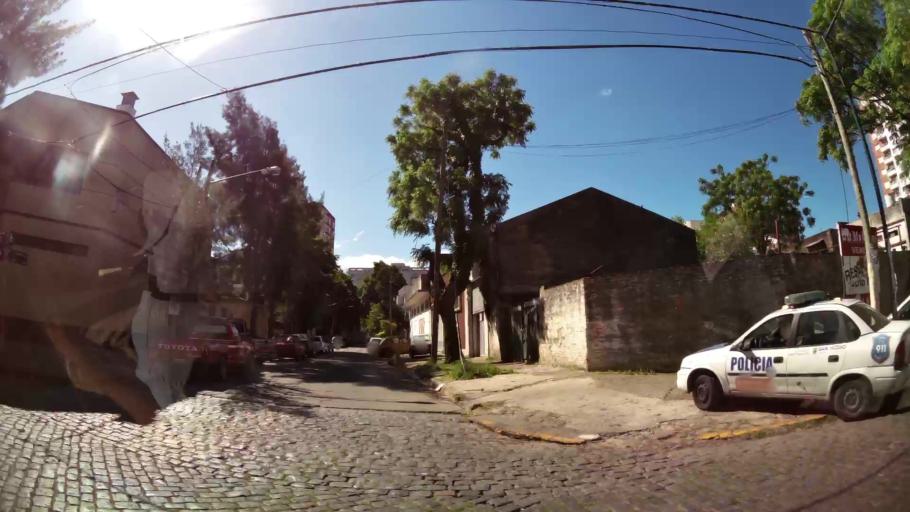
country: AR
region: Buenos Aires
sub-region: Partido de San Isidro
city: San Isidro
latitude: -34.4620
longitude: -58.5273
